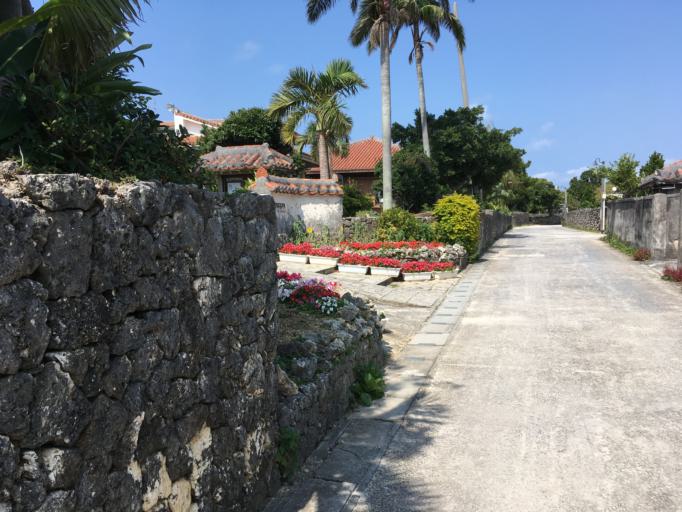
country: JP
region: Okinawa
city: Ishigaki
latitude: 24.3284
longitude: 124.0868
